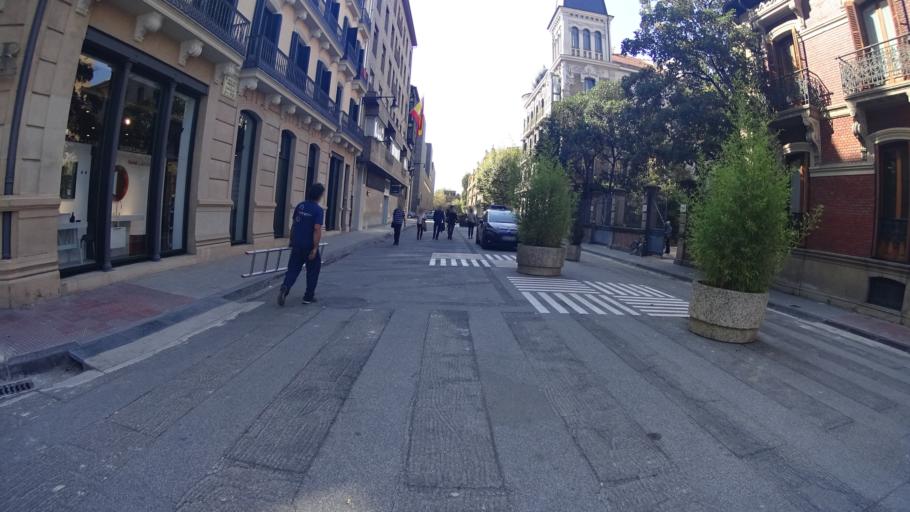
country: ES
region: Navarre
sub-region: Provincia de Navarra
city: Primer Ensanche
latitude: 42.8150
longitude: -1.6476
